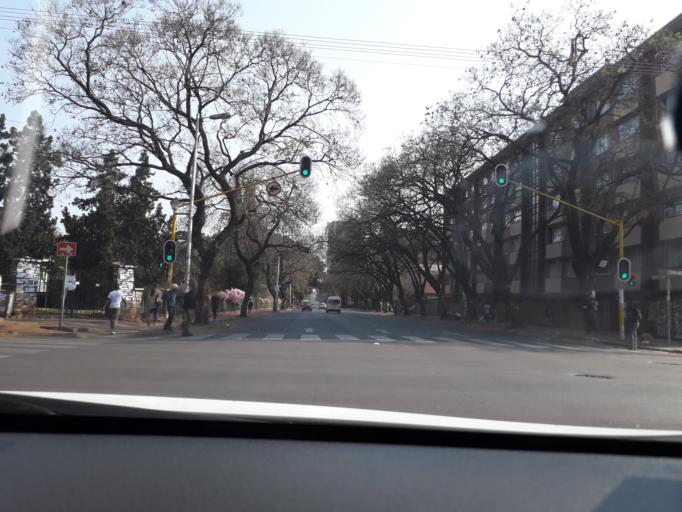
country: ZA
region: Gauteng
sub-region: City of Tshwane Metropolitan Municipality
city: Pretoria
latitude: -25.7552
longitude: 28.1937
